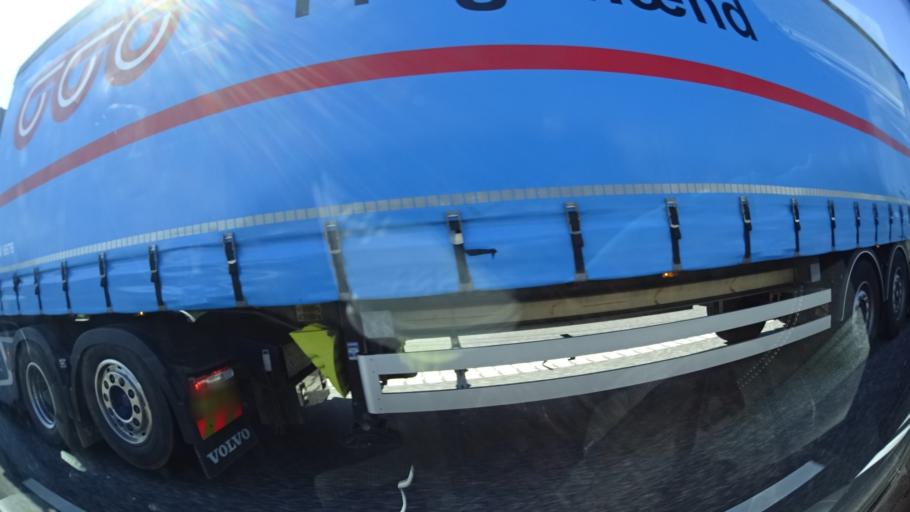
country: DK
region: Central Jutland
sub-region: Arhus Kommune
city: Sabro
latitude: 56.1901
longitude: 10.0704
